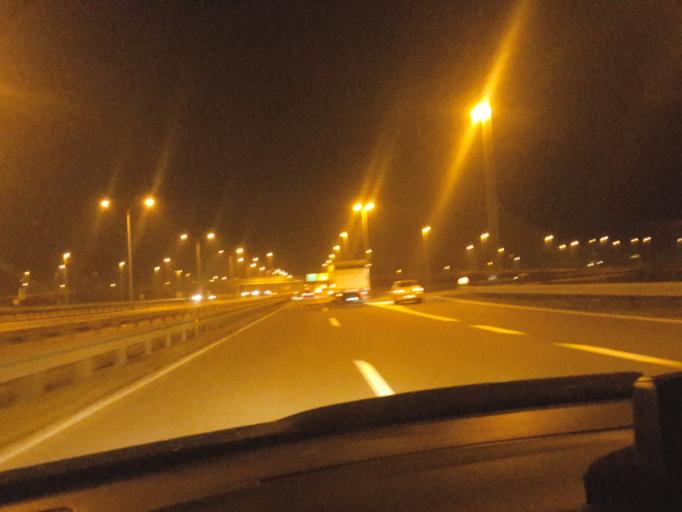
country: RS
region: Autonomna Pokrajina Vojvodina
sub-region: Juznobacki Okrug
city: Novi Sad
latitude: 45.3069
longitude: 19.8345
